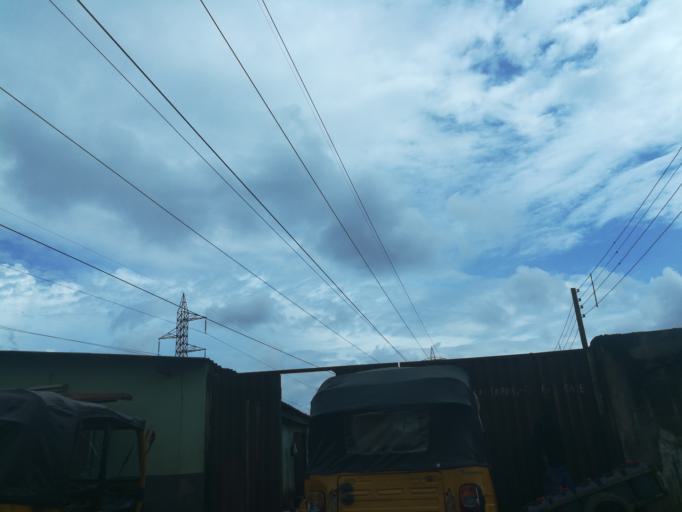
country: NG
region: Lagos
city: Agege
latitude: 6.6213
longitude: 3.3354
